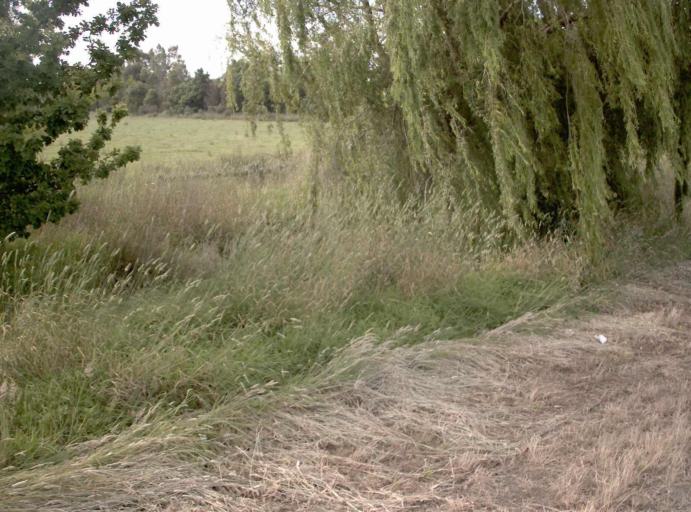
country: AU
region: Victoria
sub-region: Wellington
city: Heyfield
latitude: -38.0042
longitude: 146.7807
